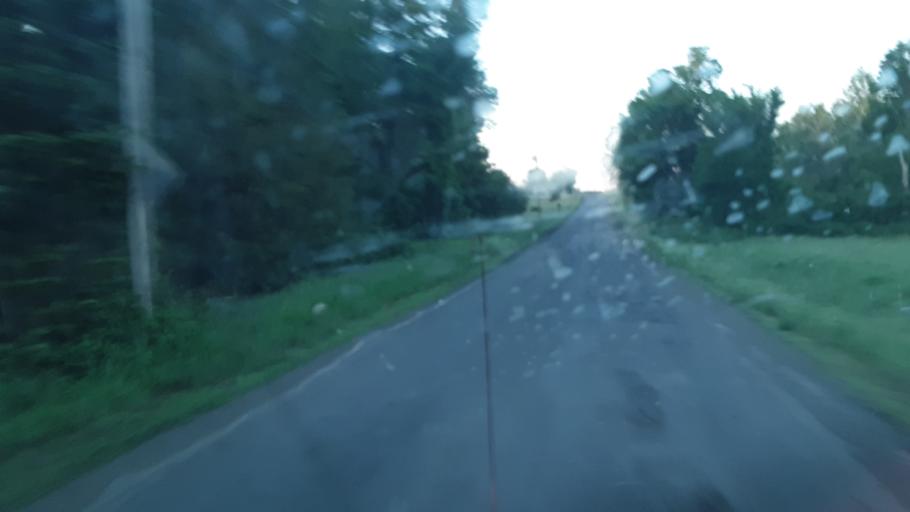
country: US
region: Maine
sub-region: Aroostook County
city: Caribou
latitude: 46.8661
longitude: -68.1374
